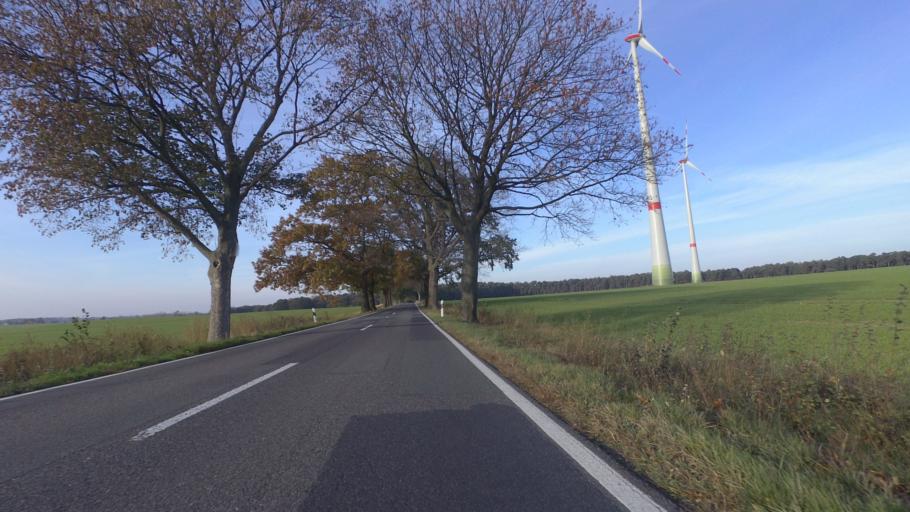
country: DE
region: Brandenburg
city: Trebbin
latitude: 52.2088
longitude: 13.3034
